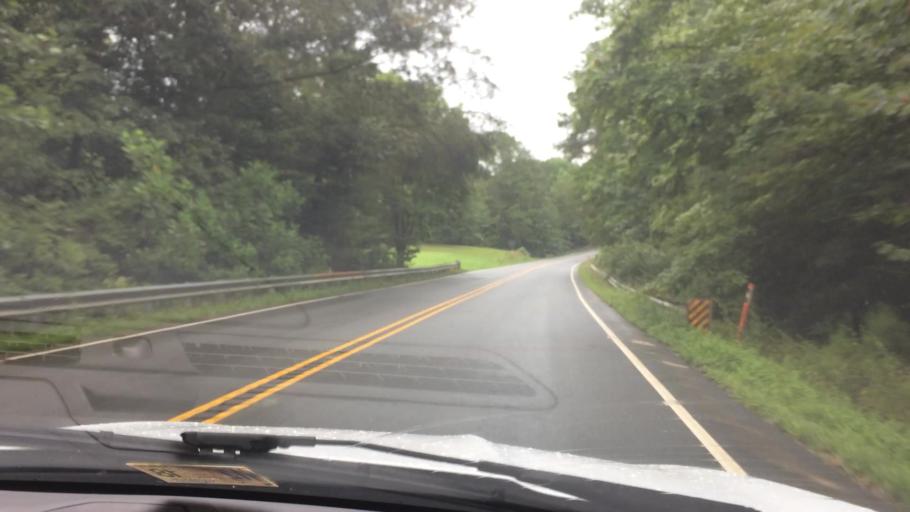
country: US
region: Virginia
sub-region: King William County
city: West Point
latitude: 37.5675
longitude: -76.7500
